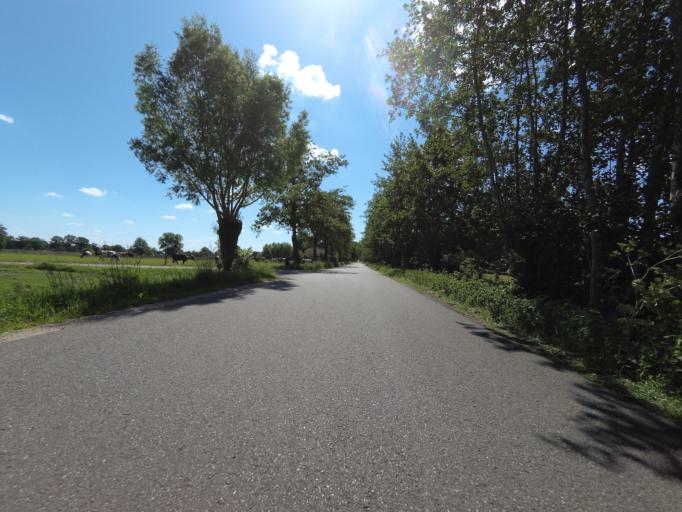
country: NL
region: Gelderland
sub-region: Gemeente Ede
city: Wekerom
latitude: 52.1138
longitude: 5.6884
